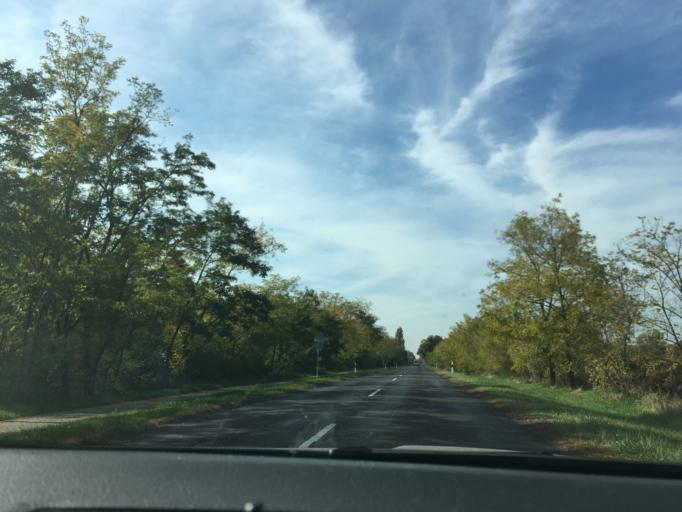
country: HU
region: Hajdu-Bihar
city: Vamospercs
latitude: 47.5257
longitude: 21.9408
